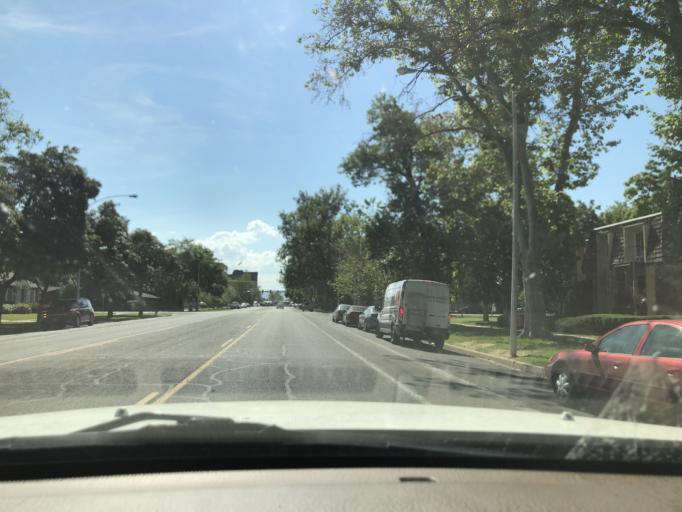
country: US
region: Utah
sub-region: Utah County
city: Provo
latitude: 40.2337
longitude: -111.6524
